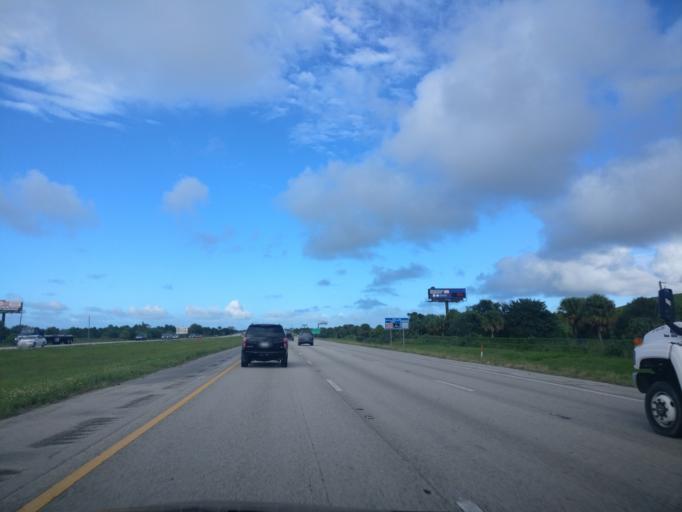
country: US
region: Florida
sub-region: Saint Lucie County
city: Fort Pierce South
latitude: 27.3904
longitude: -80.4010
